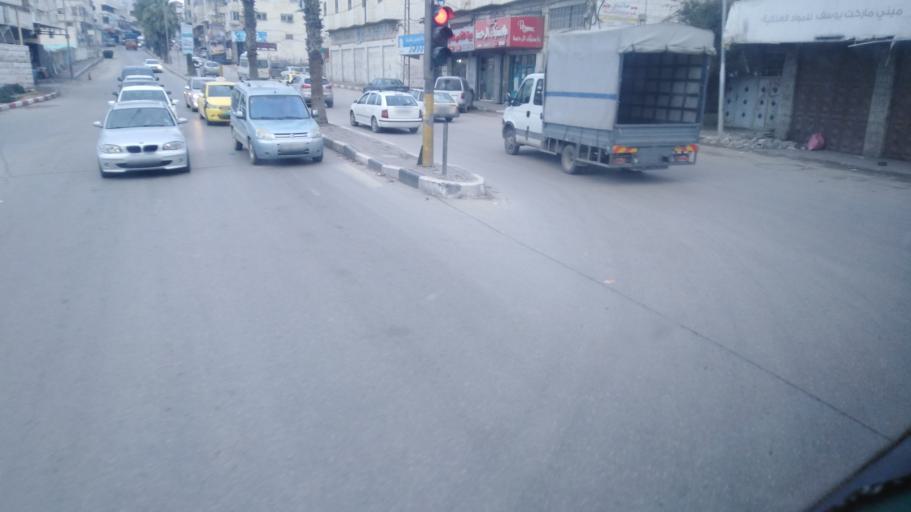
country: PS
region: West Bank
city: Hebron
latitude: 31.5312
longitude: 35.0893
